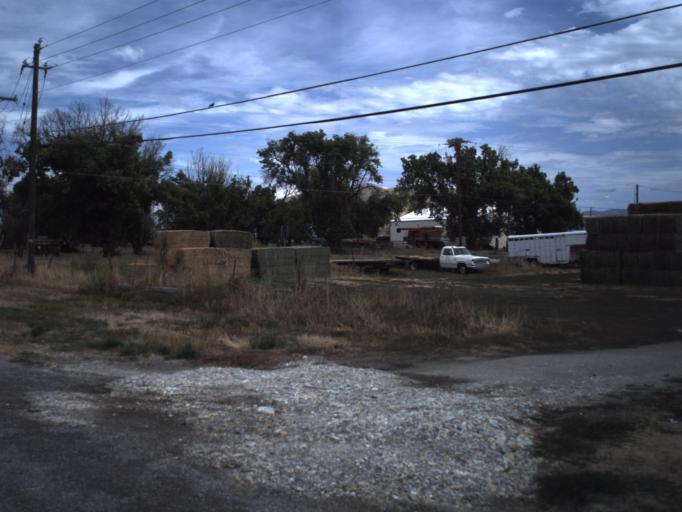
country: US
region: Utah
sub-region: Cache County
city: Benson
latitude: 41.8620
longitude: -111.9998
